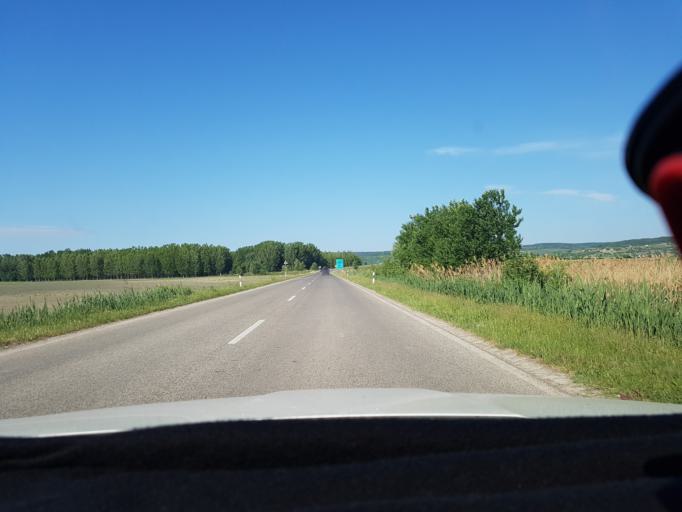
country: HU
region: Tolna
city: Ocseny
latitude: 46.3086
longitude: 18.7330
